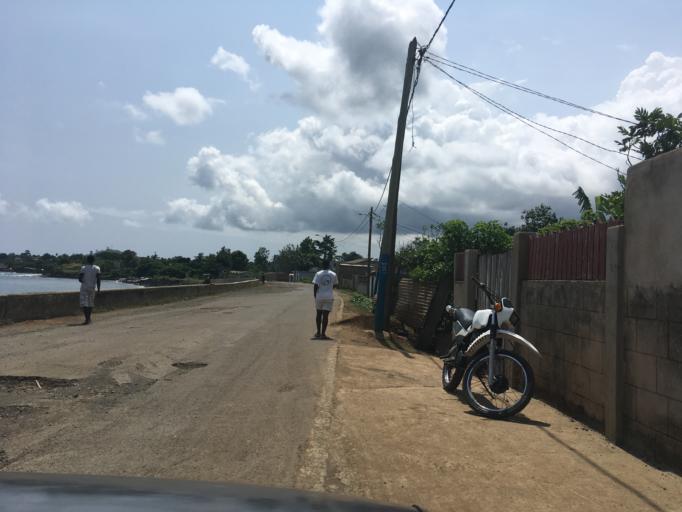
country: ST
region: Sao Tome Island
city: Sao Tome
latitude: 0.3242
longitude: 6.7407
